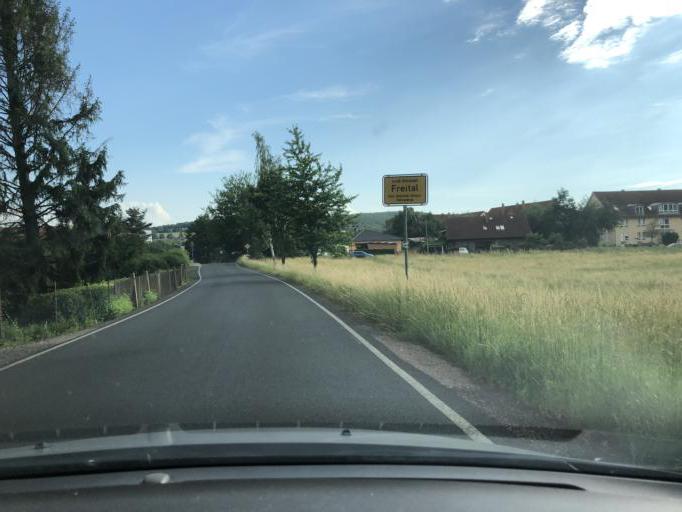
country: DE
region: Saxony
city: Freital
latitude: 51.0214
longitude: 13.6409
